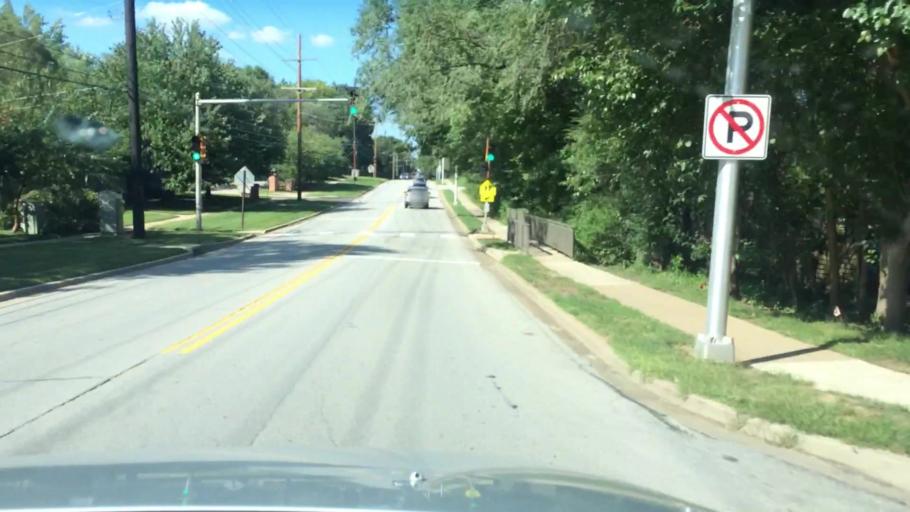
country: US
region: Kansas
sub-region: Johnson County
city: Overland Park
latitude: 38.9732
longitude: -94.6490
